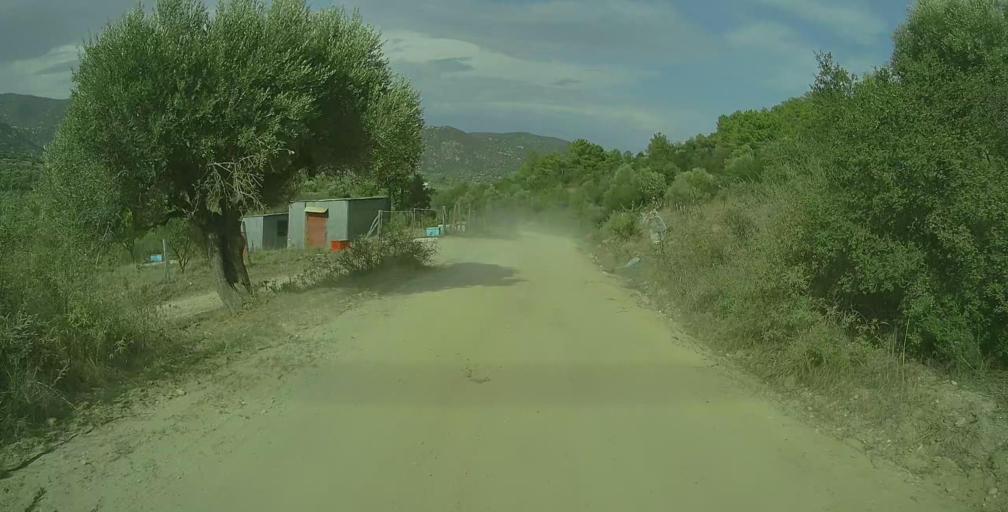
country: GR
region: Central Macedonia
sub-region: Nomos Chalkidikis
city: Sykia
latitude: 40.0252
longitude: 23.9461
